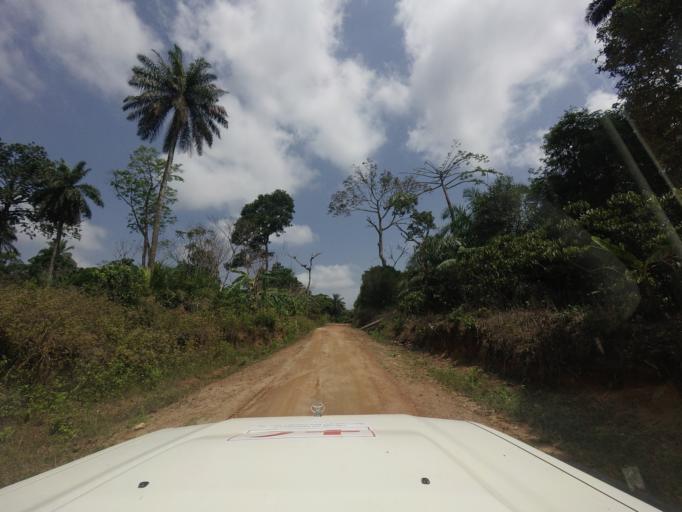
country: LR
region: Lofa
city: Voinjama
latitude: 8.4801
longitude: -9.6627
